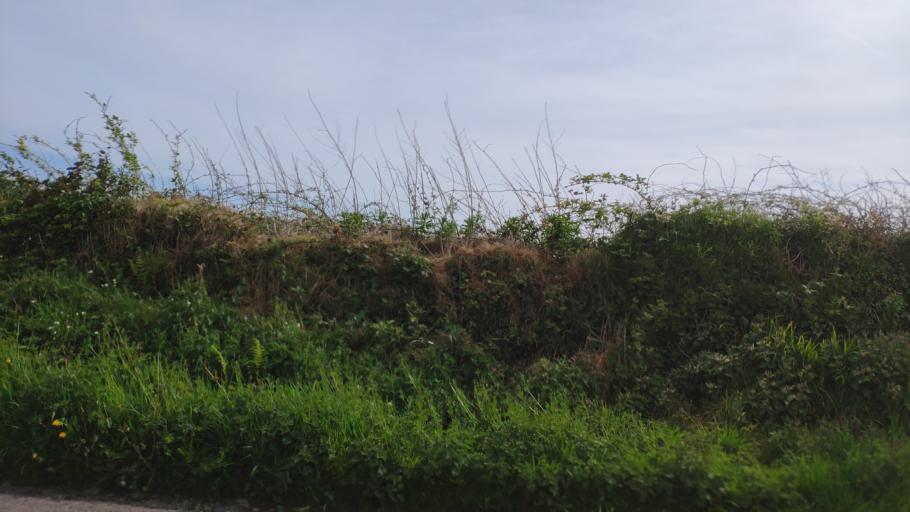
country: IE
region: Munster
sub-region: County Cork
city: Blarney
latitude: 51.9613
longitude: -8.5136
